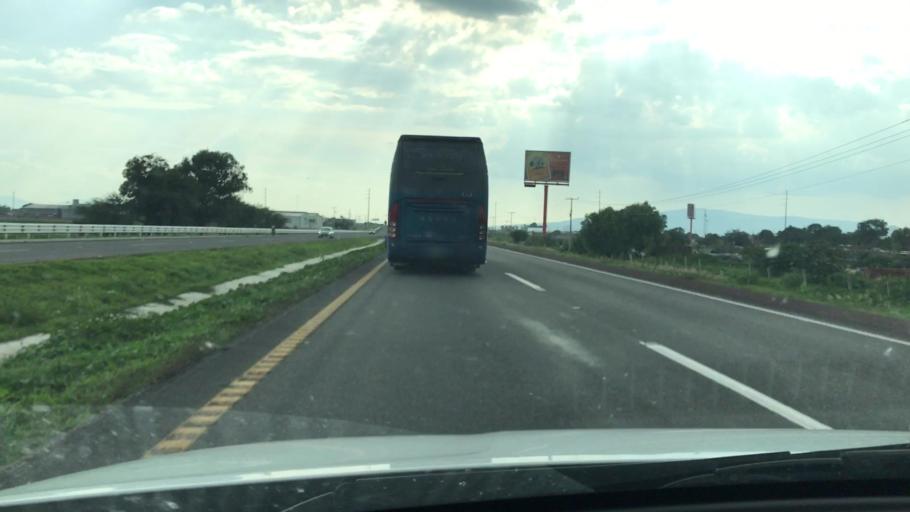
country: MX
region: Guanajuato
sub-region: Irapuato
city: Las Huertas Tercera Seccion
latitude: 20.6496
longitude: -101.3672
